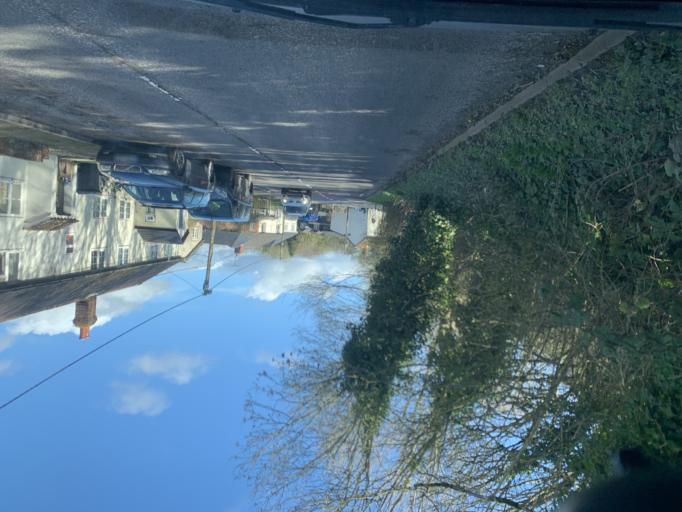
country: GB
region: England
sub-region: Wiltshire
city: Stockton
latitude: 51.1934
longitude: -2.0096
